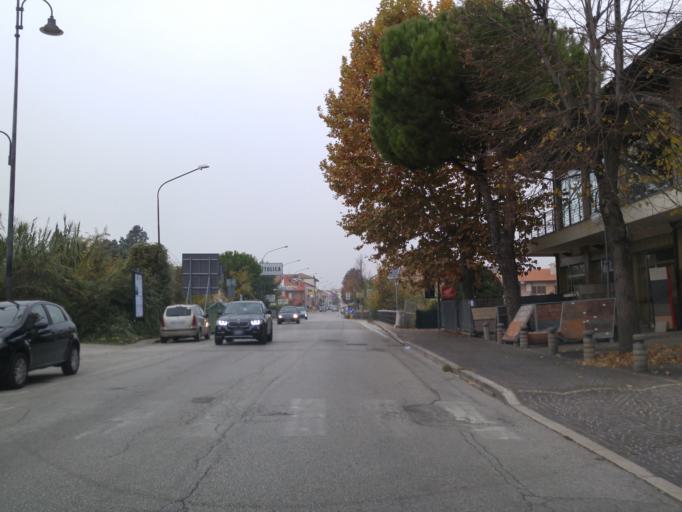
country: IT
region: The Marches
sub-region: Provincia di Pesaro e Urbino
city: Gabicce Mare
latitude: 43.9598
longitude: 12.7539
